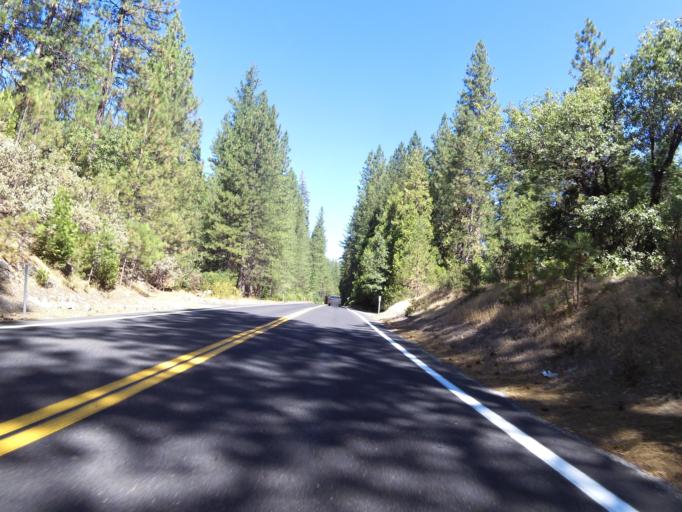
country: US
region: California
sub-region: Calaveras County
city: Arnold
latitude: 38.2136
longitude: -120.3696
